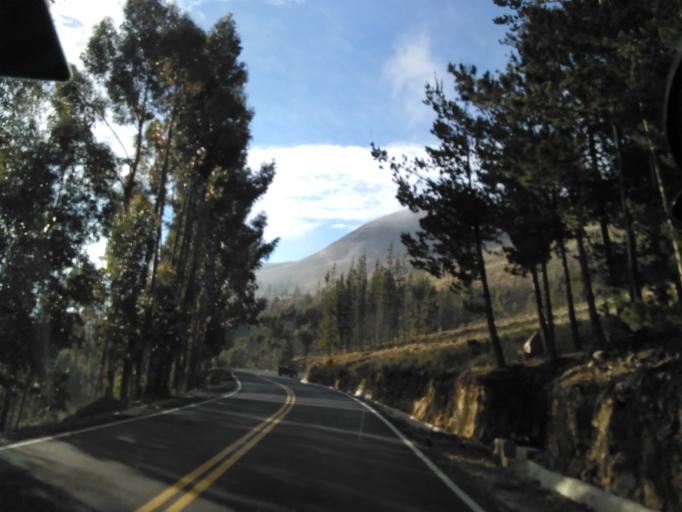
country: BO
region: Cochabamba
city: Arani
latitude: -17.6912
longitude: -65.5694
